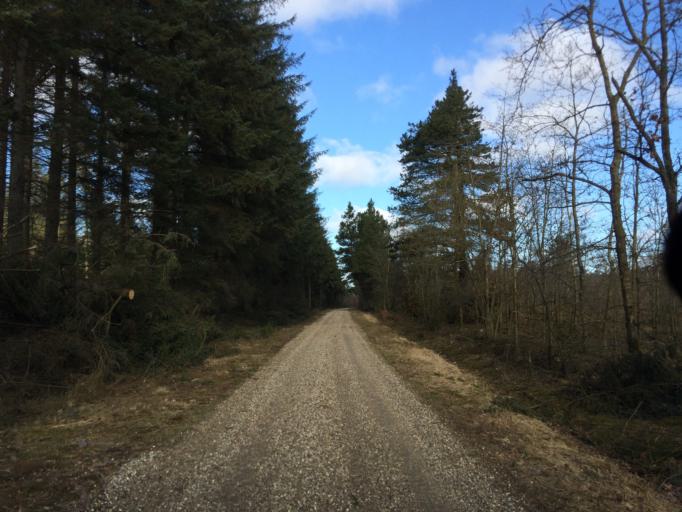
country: DK
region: Central Jutland
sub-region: Holstebro Kommune
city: Ulfborg
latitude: 56.2749
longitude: 8.4241
